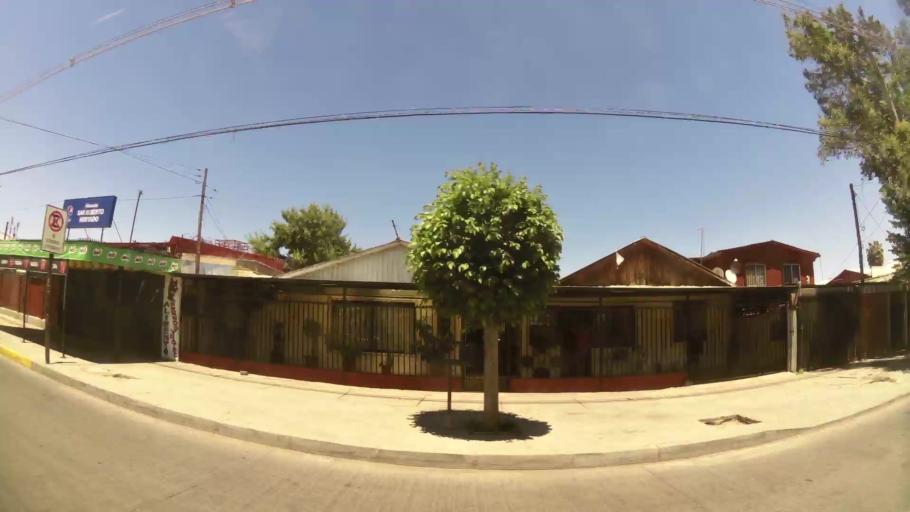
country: CL
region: Santiago Metropolitan
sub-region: Provincia de Maipo
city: San Bernardo
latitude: -33.6102
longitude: -70.6994
